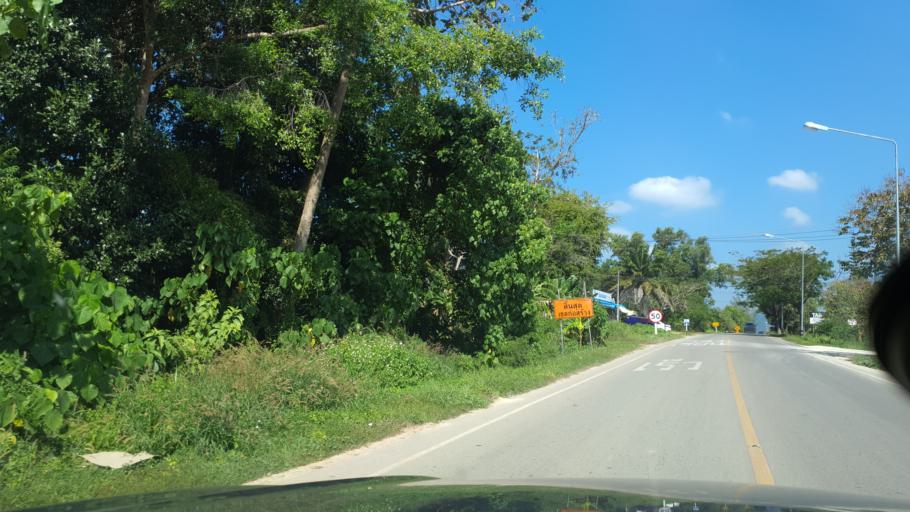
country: TH
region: Phangnga
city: Ban Ao Nang
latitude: 8.0386
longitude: 98.8617
